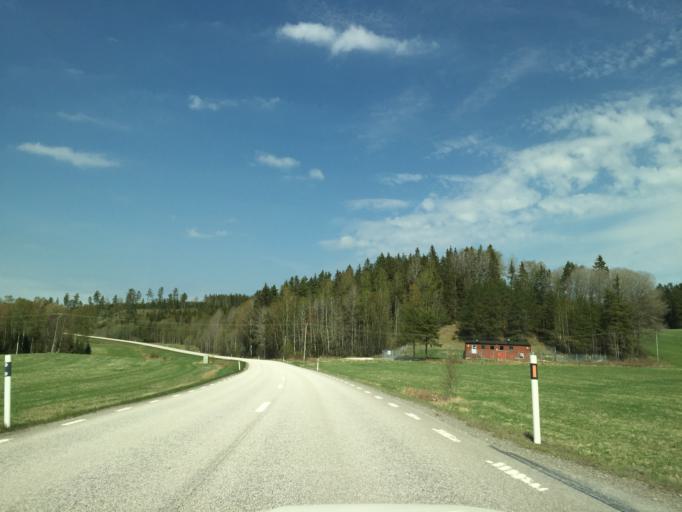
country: SE
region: Vaestra Goetaland
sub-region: Bengtsfors Kommun
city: Billingsfors
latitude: 58.9159
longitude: 12.2230
